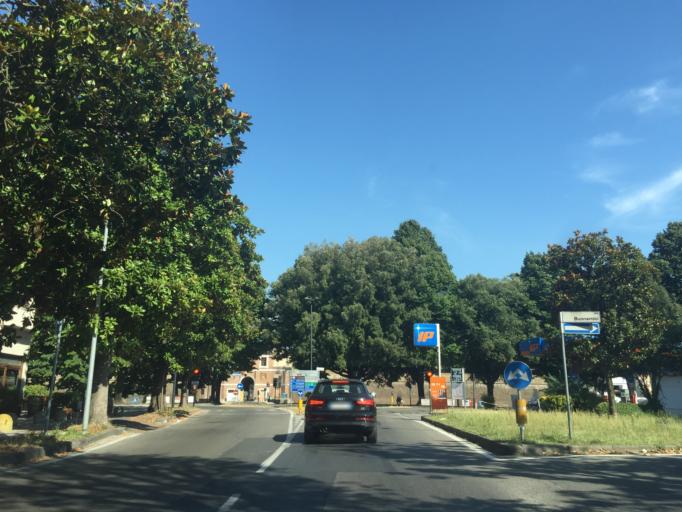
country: IT
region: Tuscany
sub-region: Provincia di Lucca
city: Lucca
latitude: 43.8452
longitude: 10.4946
